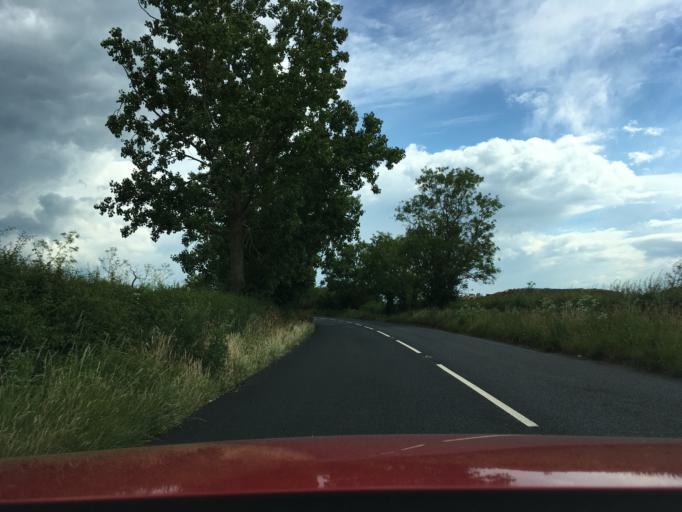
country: GB
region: England
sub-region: Gloucestershire
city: Stonehouse
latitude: 51.7892
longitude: -2.2897
